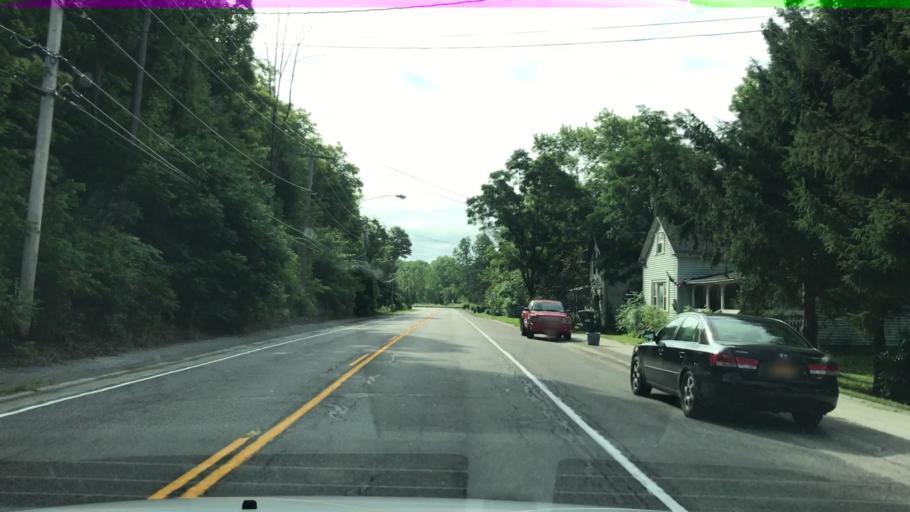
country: US
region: New York
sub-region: Erie County
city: Alden
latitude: 42.8423
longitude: -78.4671
